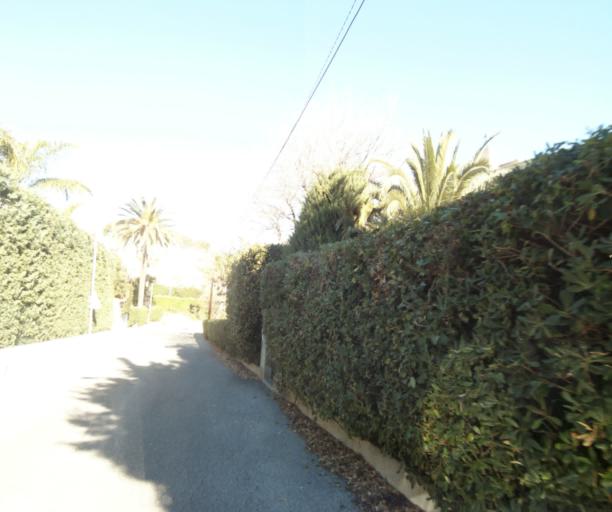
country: FR
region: Provence-Alpes-Cote d'Azur
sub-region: Departement des Alpes-Maritimes
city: Antibes
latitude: 43.5718
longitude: 7.1203
